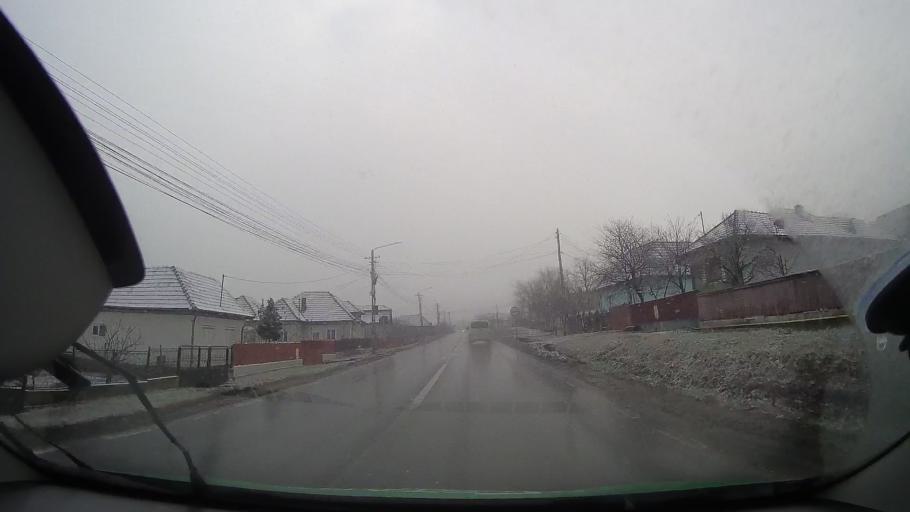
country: RO
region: Mures
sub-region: Comuna Bagaciu
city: Delenii
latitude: 46.2831
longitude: 24.3007
